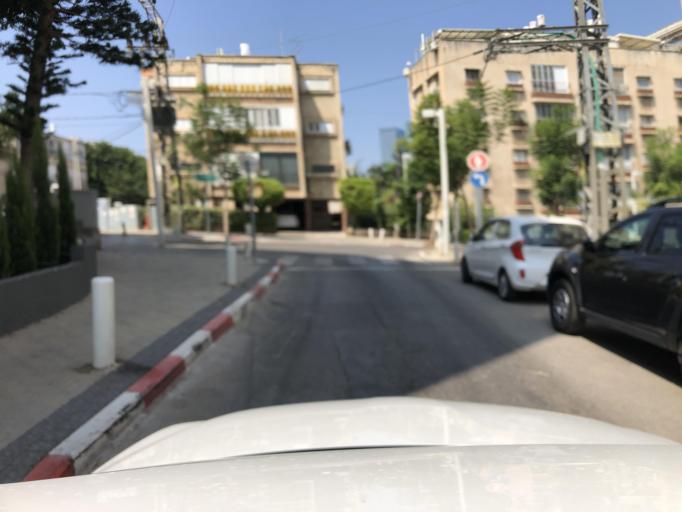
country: IL
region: Tel Aviv
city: Ramat Gan
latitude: 32.0768
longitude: 34.8048
